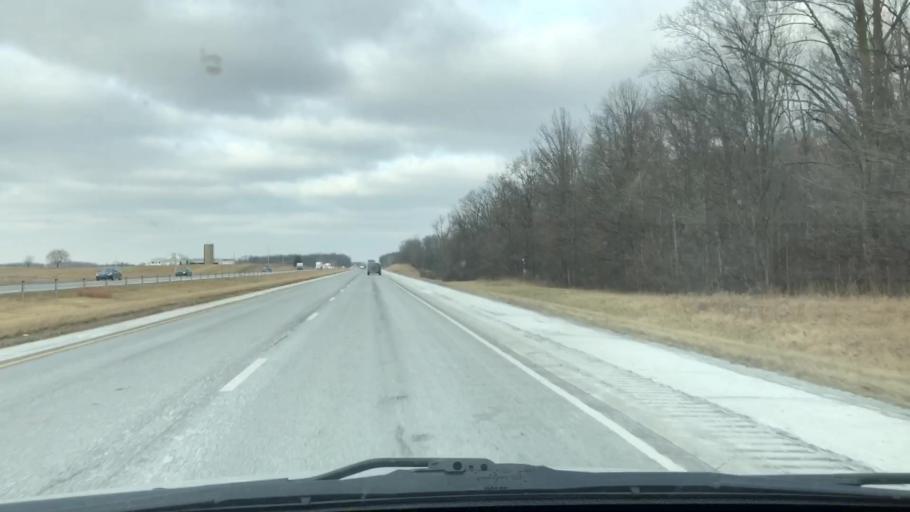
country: US
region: Indiana
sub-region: DeKalb County
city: Waterloo
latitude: 41.4513
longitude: -85.0540
